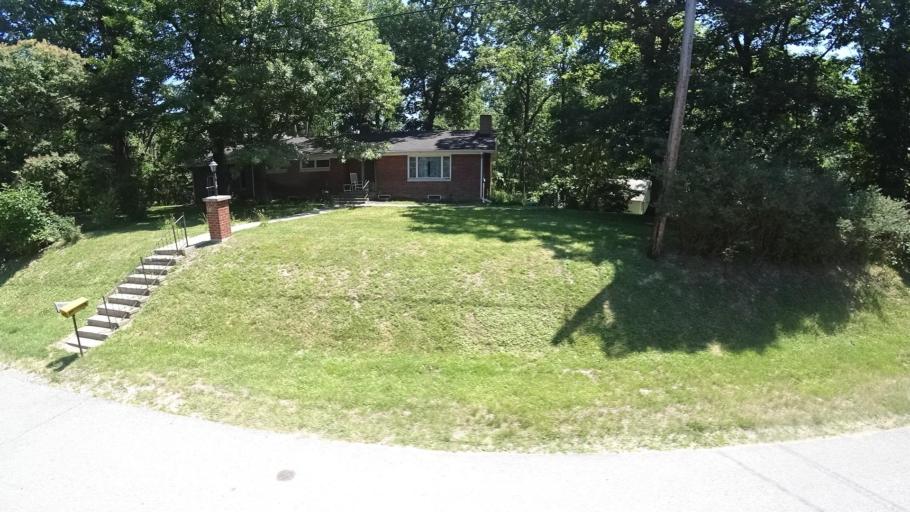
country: US
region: Indiana
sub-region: Porter County
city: Burns Harbor
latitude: 41.6055
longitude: -87.1394
